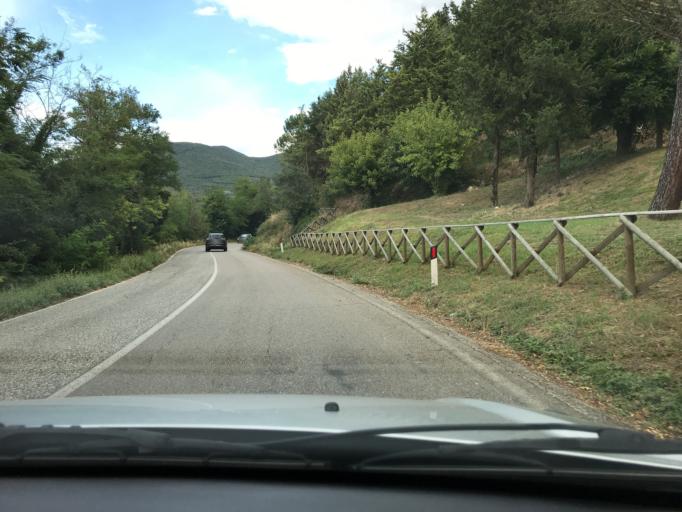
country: IT
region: Umbria
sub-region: Provincia di Terni
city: Montecchio
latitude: 42.6636
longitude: 12.2839
